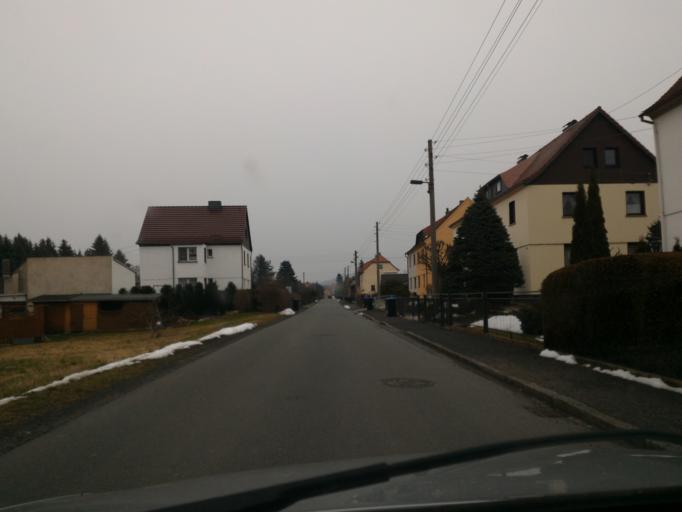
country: DE
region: Saxony
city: Grossschonau
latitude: 50.8859
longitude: 14.6524
